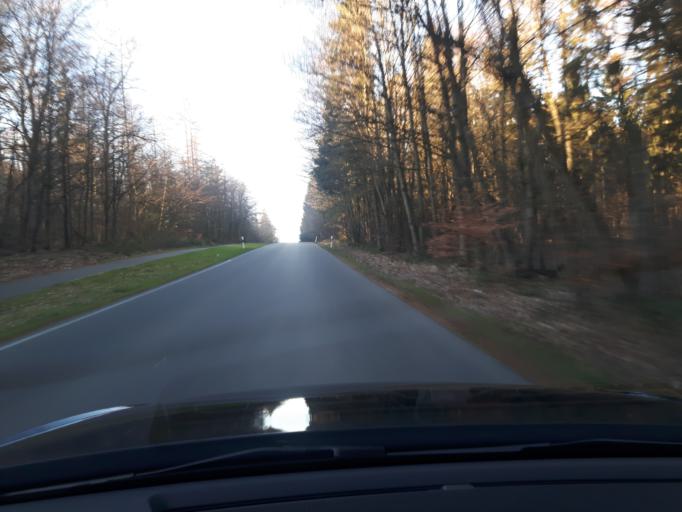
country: DE
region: Mecklenburg-Vorpommern
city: Sehlen
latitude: 54.3796
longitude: 13.4054
